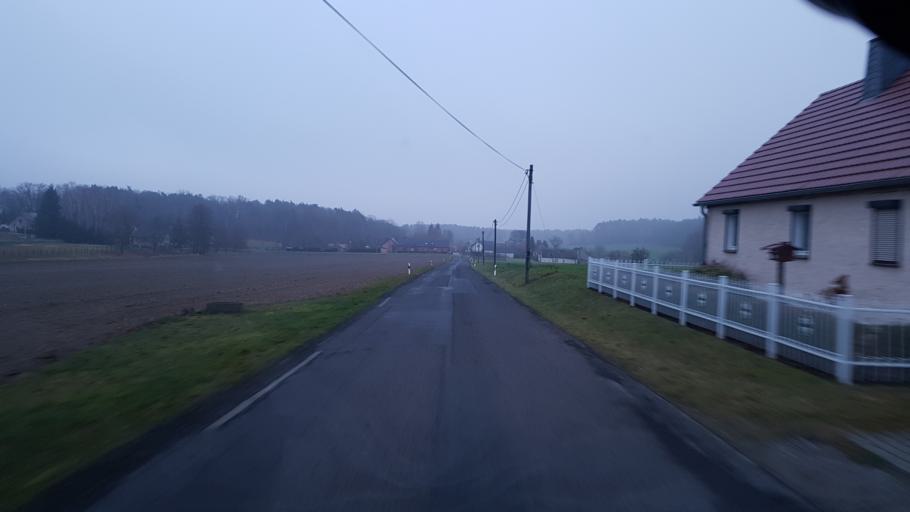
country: DE
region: Brandenburg
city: Bronkow
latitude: 51.6870
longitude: 13.9568
